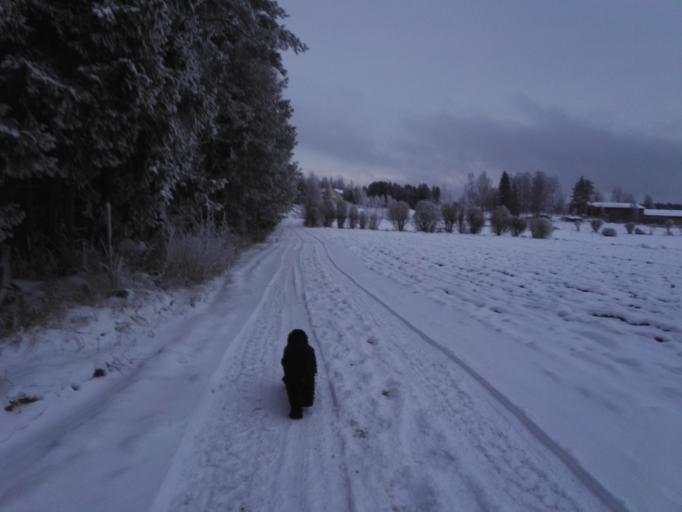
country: FI
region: Satakunta
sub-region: Pohjois-Satakunta
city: Jaemijaervi
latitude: 61.7842
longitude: 22.8749
